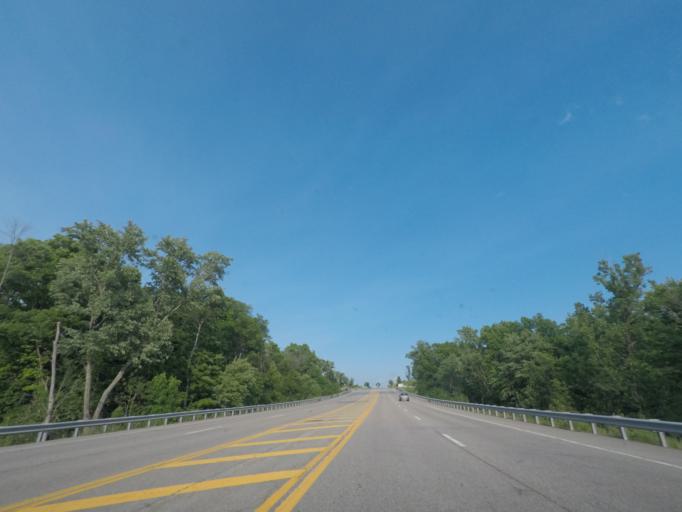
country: US
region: New York
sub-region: Orange County
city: Orange Lake
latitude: 41.4971
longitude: -74.1123
